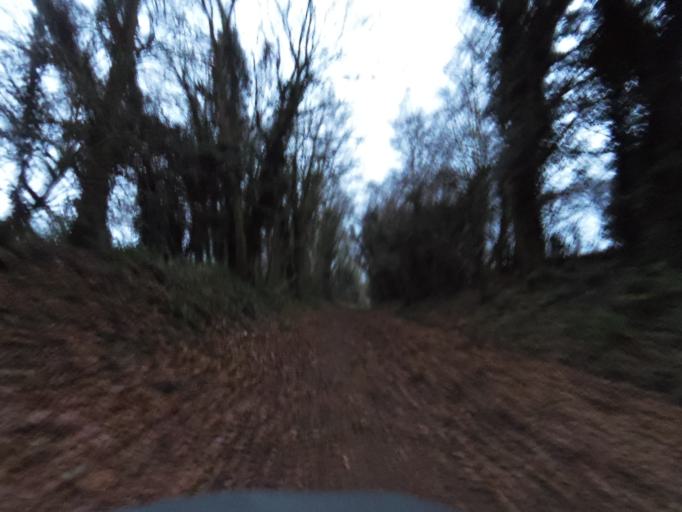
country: GB
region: England
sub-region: Norfolk
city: Costessey
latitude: 52.6823
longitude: 1.2154
